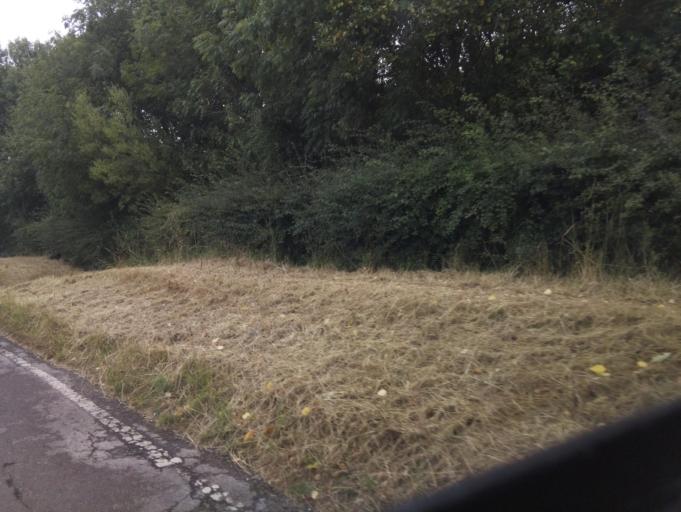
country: GB
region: England
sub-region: Derbyshire
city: Findern
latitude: 52.8889
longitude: -1.5196
